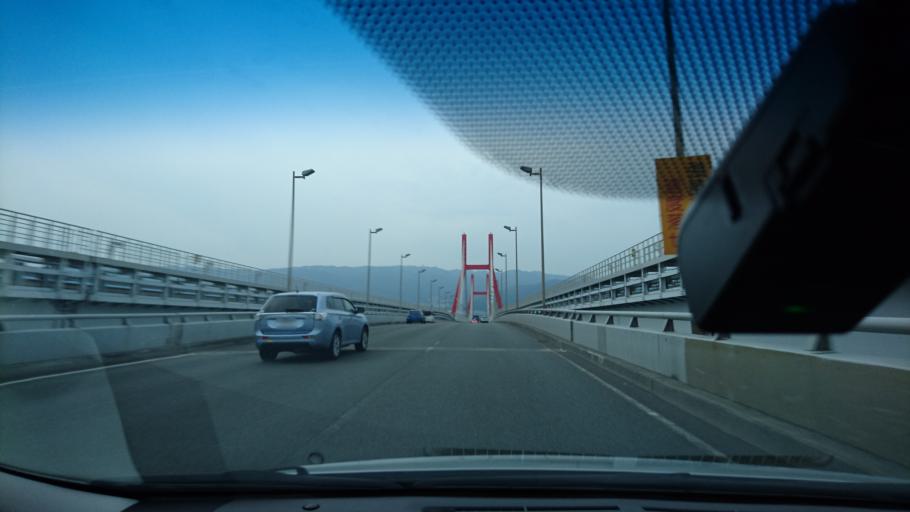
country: JP
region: Hyogo
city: Ashiya
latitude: 34.6962
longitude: 135.2683
